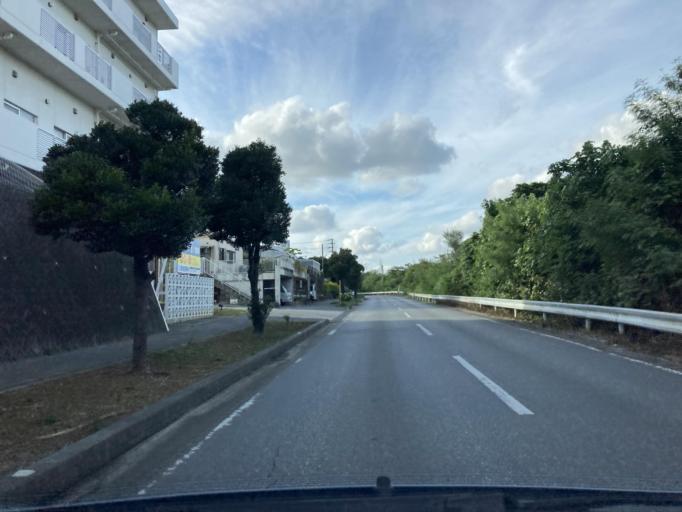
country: JP
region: Okinawa
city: Itoman
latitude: 26.1320
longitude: 127.7550
